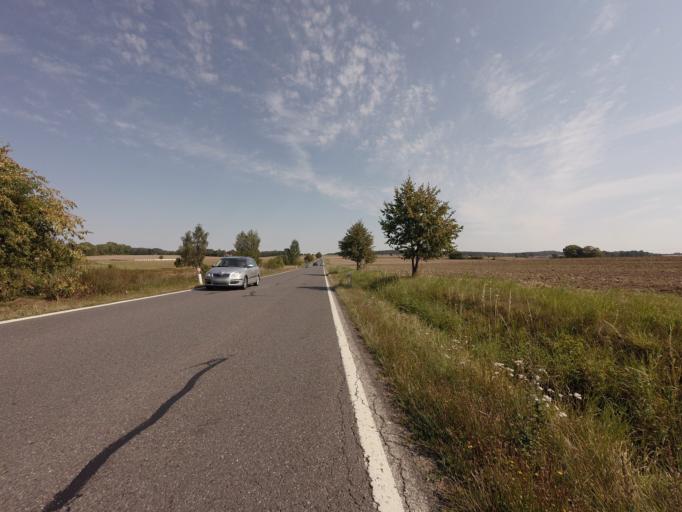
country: CZ
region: Jihocesky
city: Bernartice
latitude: 49.3928
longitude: 14.3604
